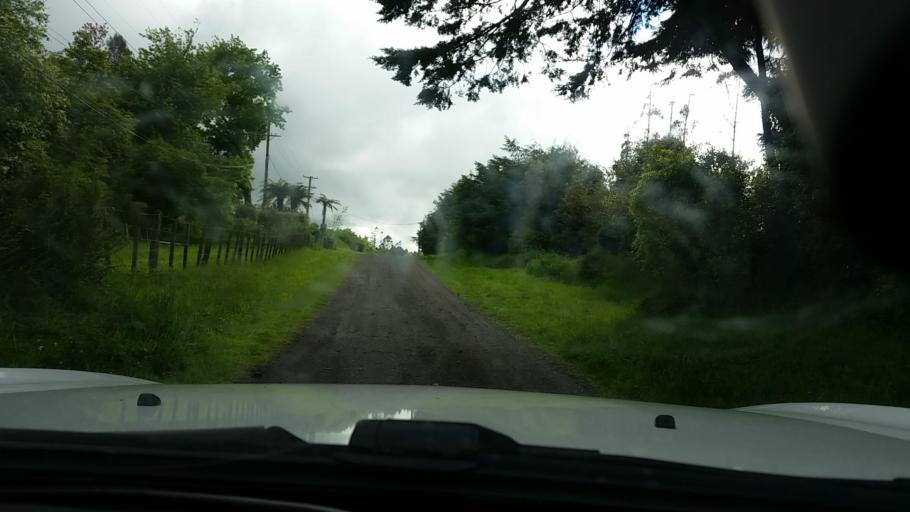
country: NZ
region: Bay of Plenty
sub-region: Rotorua District
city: Rotorua
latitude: -38.1012
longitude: 176.0797
